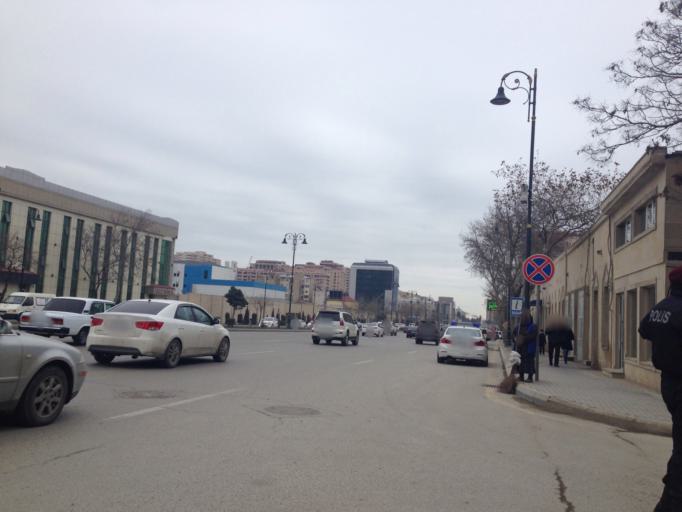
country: AZ
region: Baki
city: Baku
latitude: 40.3866
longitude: 49.8630
